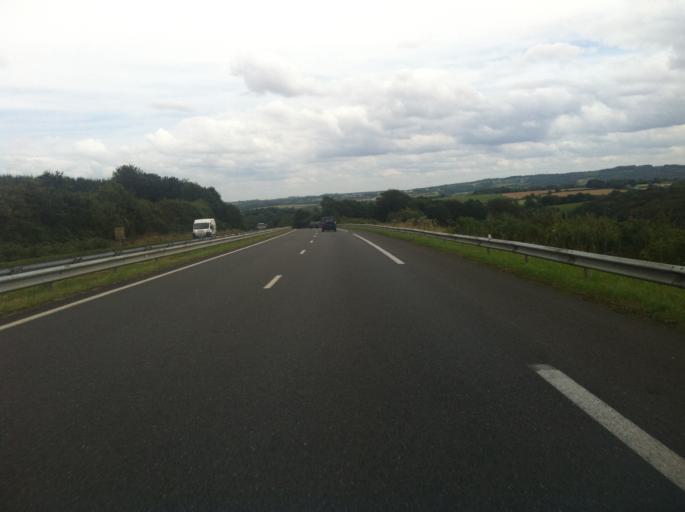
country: FR
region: Brittany
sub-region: Departement du Finistere
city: Plouigneau
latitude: 48.5714
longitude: -3.6733
